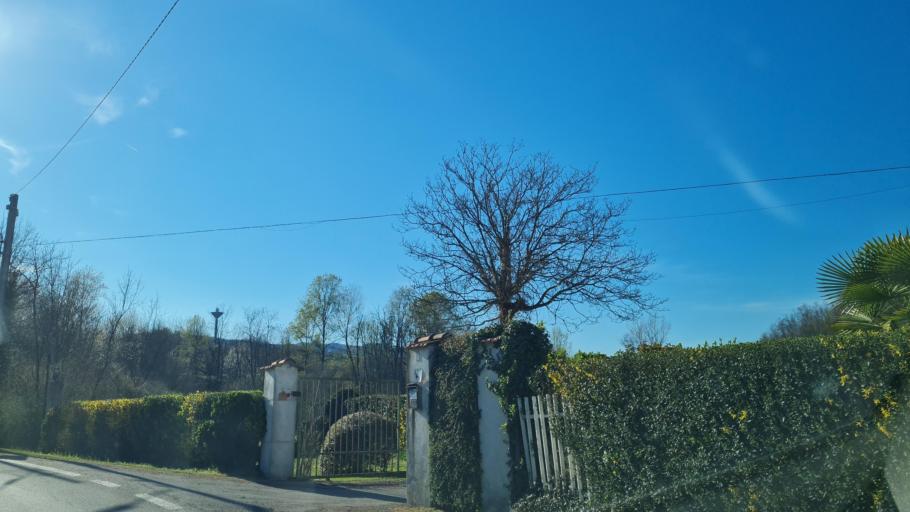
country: IT
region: Piedmont
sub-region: Provincia di Novara
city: Maggiora
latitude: 45.6944
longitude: 8.4267
